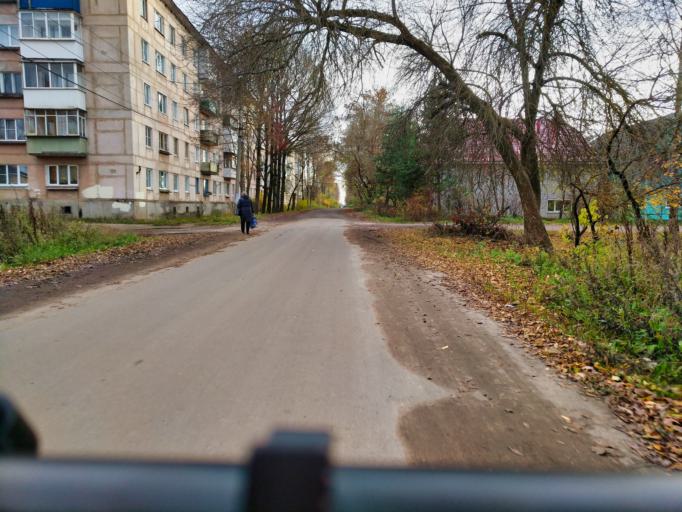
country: RU
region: Tverskaya
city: Rzhev
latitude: 56.2690
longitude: 34.3262
